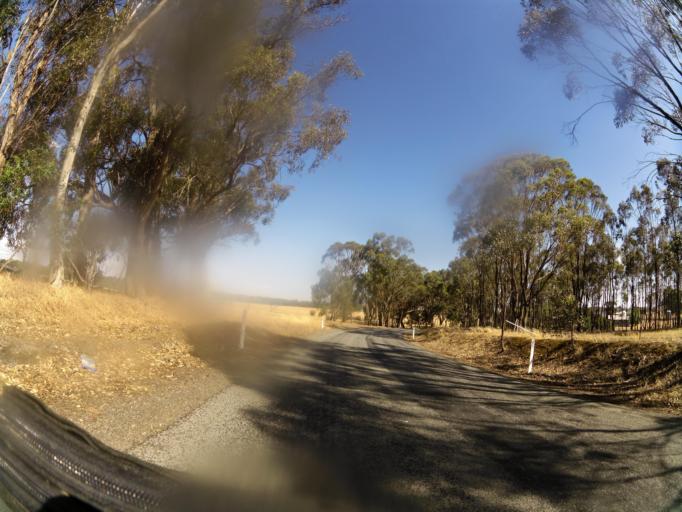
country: AU
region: Victoria
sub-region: Campaspe
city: Kyabram
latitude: -36.8916
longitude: 145.1062
